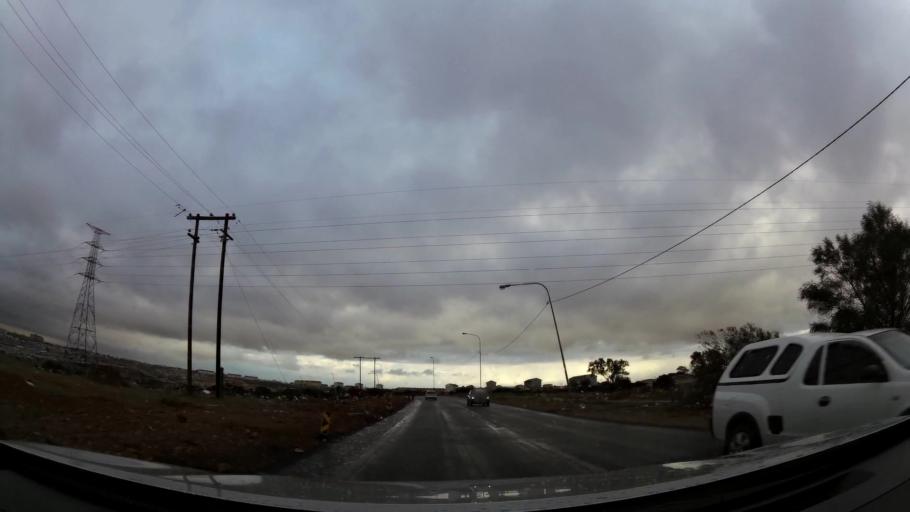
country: ZA
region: Eastern Cape
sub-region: Nelson Mandela Bay Metropolitan Municipality
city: Port Elizabeth
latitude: -33.8947
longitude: 25.5497
